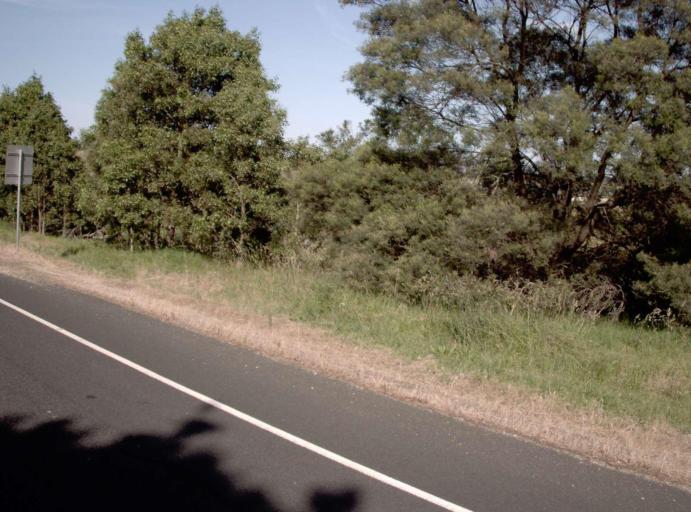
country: AU
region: Victoria
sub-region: East Gippsland
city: Lakes Entrance
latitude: -37.8486
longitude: 147.8492
